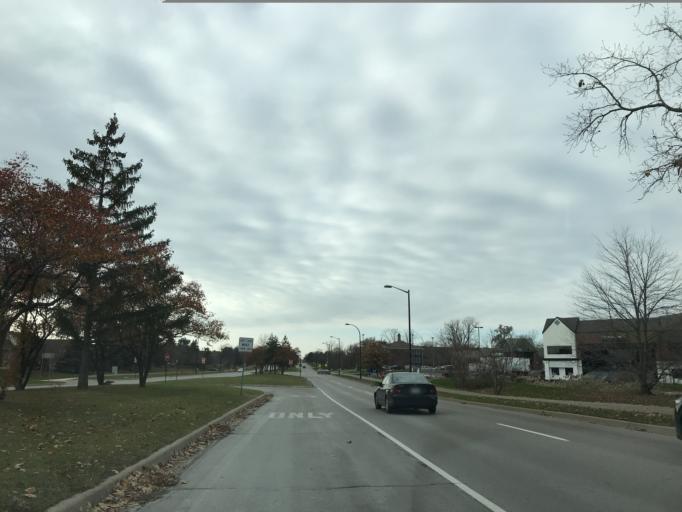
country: US
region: Michigan
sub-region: Washtenaw County
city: Ann Arbor
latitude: 42.2440
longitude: -83.7404
